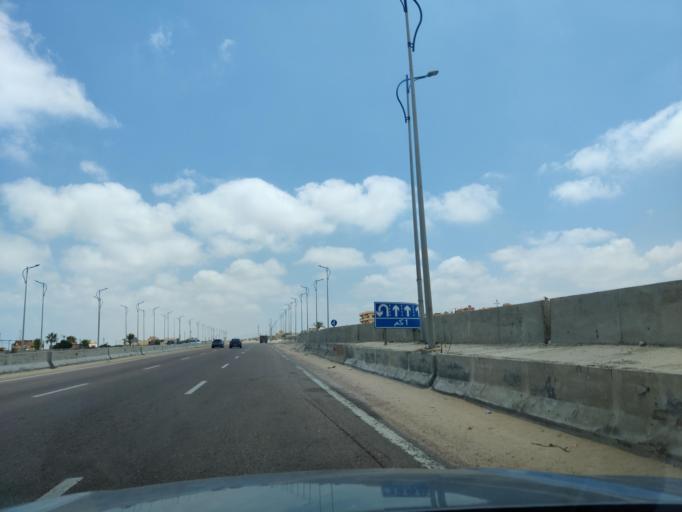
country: EG
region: Alexandria
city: Alexandria
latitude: 30.9603
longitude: 29.5426
